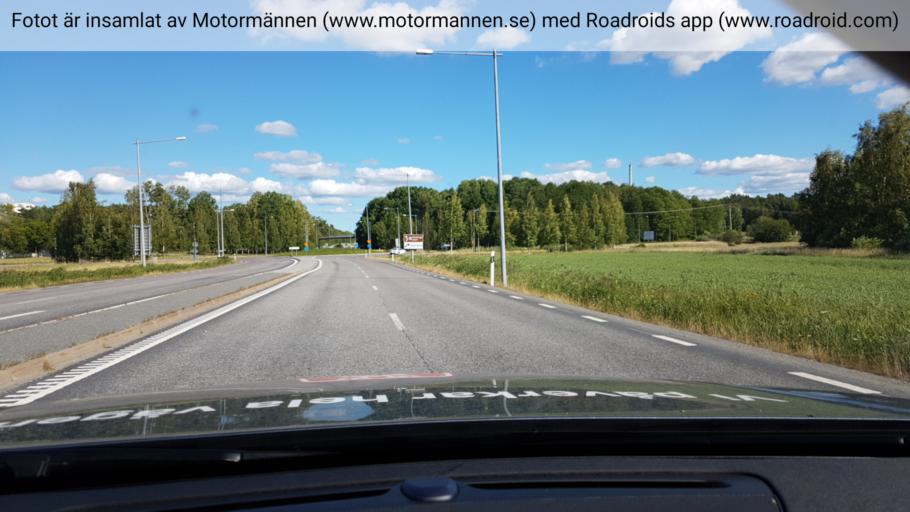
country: SE
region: Stockholm
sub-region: Sigtuna Kommun
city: Marsta
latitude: 59.6270
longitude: 17.8202
